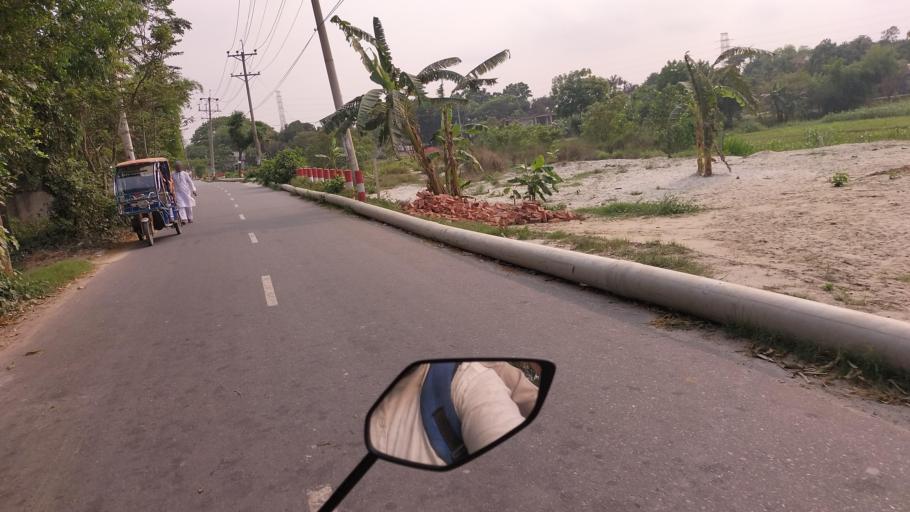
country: BD
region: Dhaka
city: Azimpur
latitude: 23.6681
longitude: 90.3415
